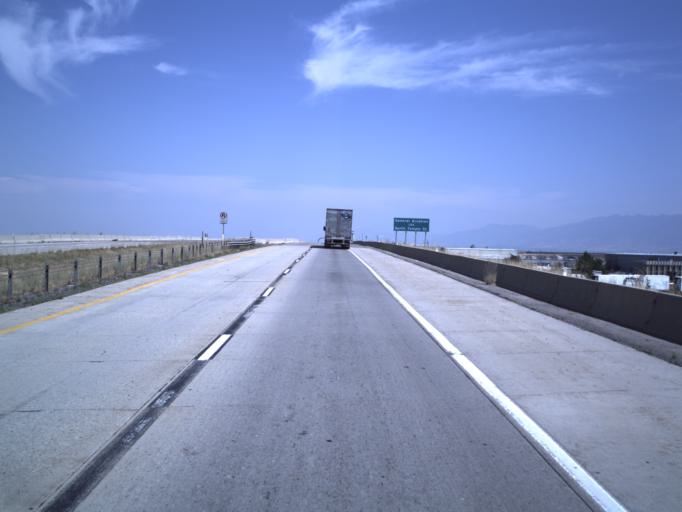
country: US
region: Utah
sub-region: Salt Lake County
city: West Valley City
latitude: 40.7515
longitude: -111.9867
